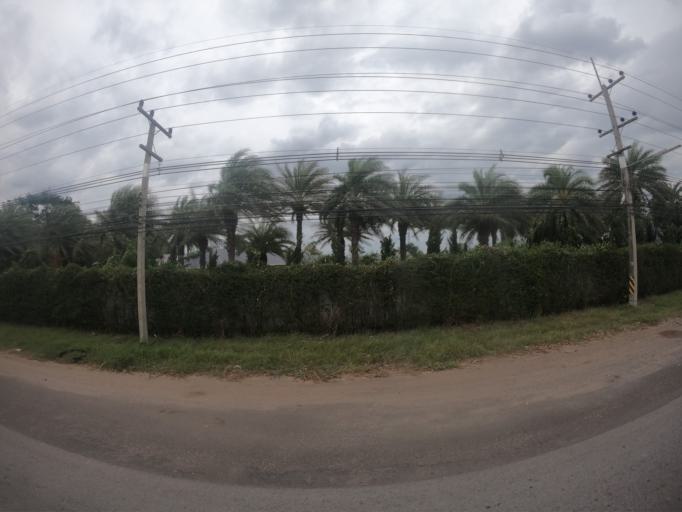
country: TH
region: Nakhon Ratchasima
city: Chok Chai
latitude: 14.7652
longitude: 102.1629
